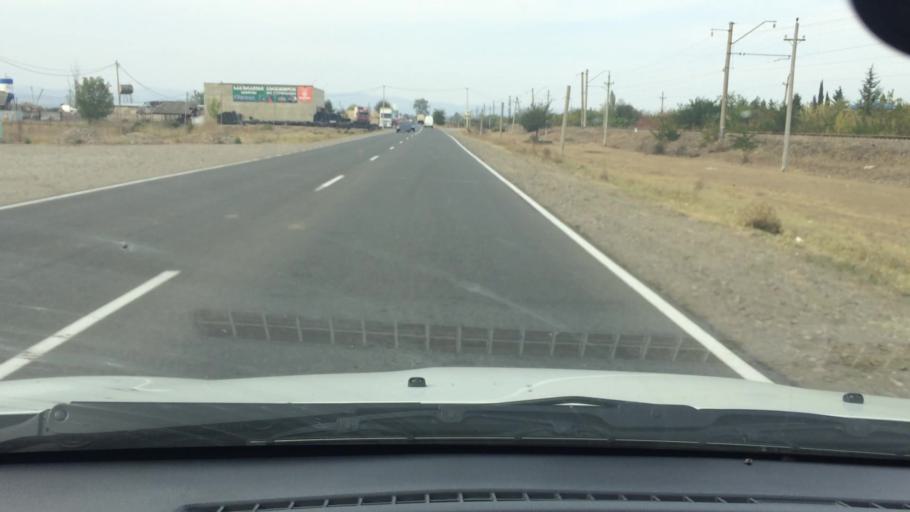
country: GE
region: Kvemo Kartli
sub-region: Marneuli
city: Marneuli
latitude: 41.4353
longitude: 44.8195
